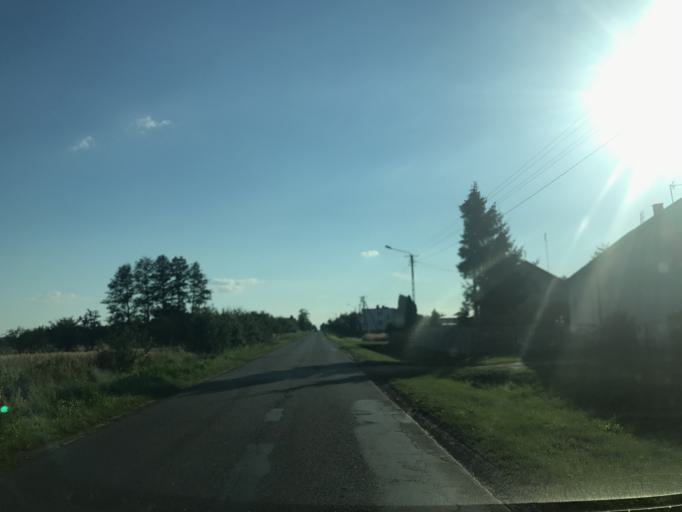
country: PL
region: Greater Poland Voivodeship
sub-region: Powiat turecki
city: Tuliszkow
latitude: 52.0831
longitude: 18.3273
